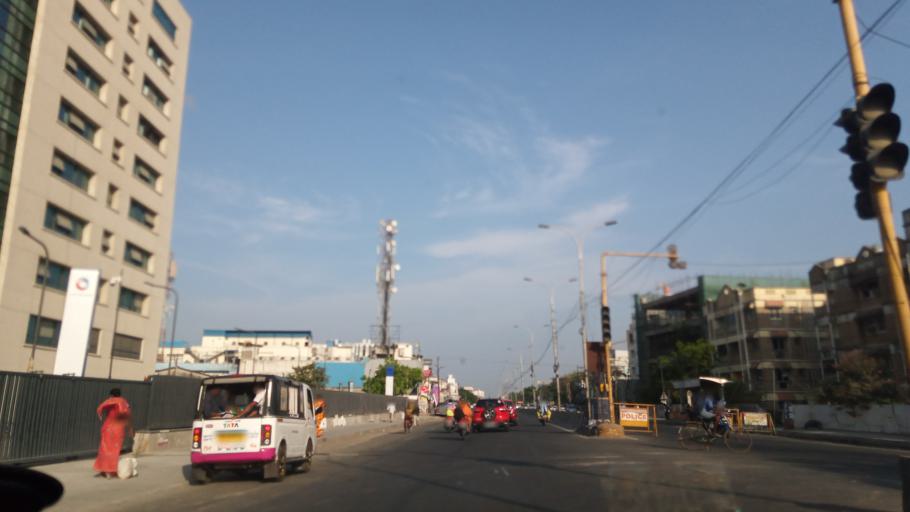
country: IN
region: Tamil Nadu
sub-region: Thiruvallur
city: Porur
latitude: 13.0294
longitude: 80.1687
